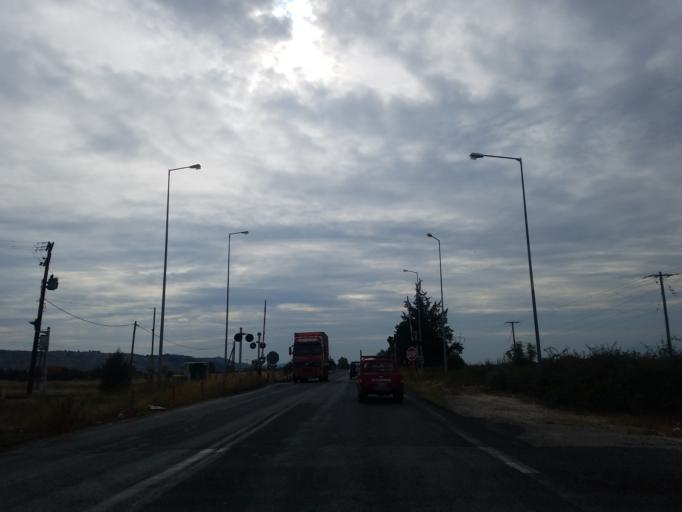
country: GR
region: Thessaly
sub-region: Trikala
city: Vasiliki
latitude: 39.6617
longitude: 21.6737
